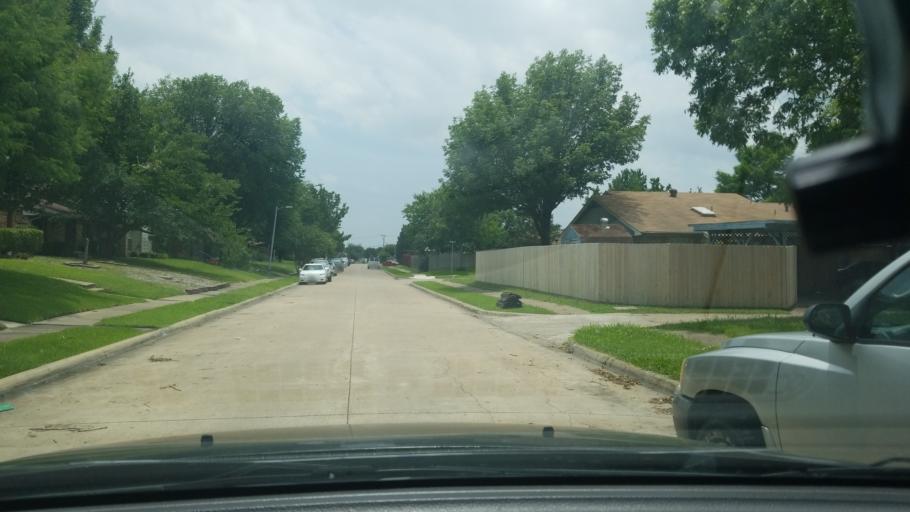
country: US
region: Texas
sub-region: Dallas County
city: Mesquite
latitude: 32.7981
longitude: -96.6164
